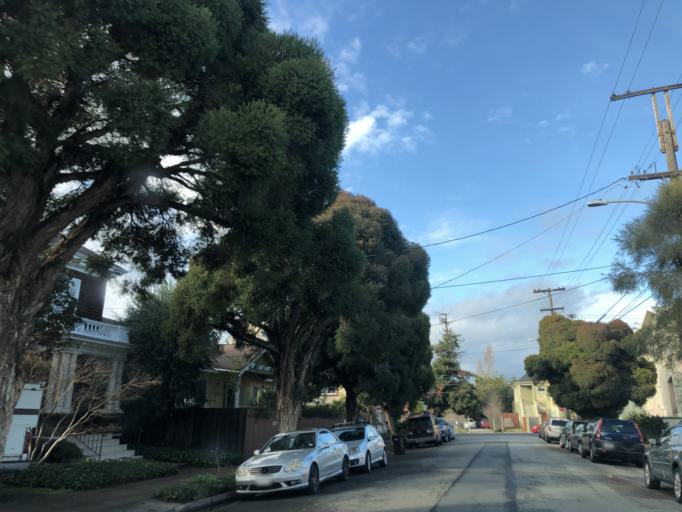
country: US
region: California
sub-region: Alameda County
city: Berkeley
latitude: 37.8493
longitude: -122.2628
